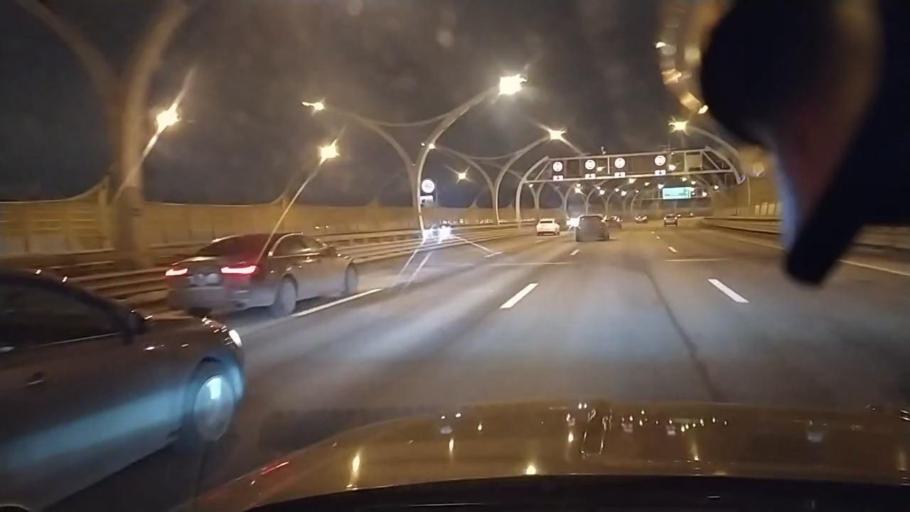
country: RU
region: St.-Petersburg
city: Staraya Derevnya
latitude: 59.9849
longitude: 30.2297
